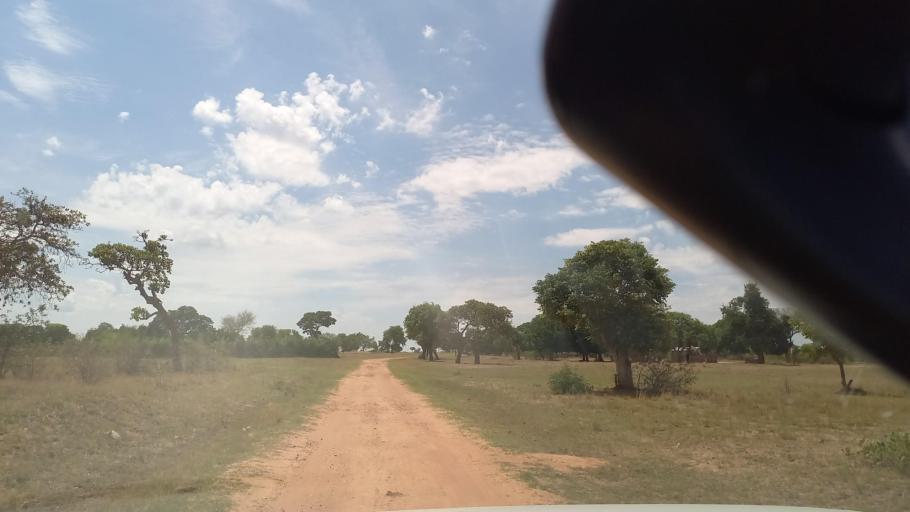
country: ZM
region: Southern
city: Mazabuka
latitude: -16.1496
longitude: 27.7778
